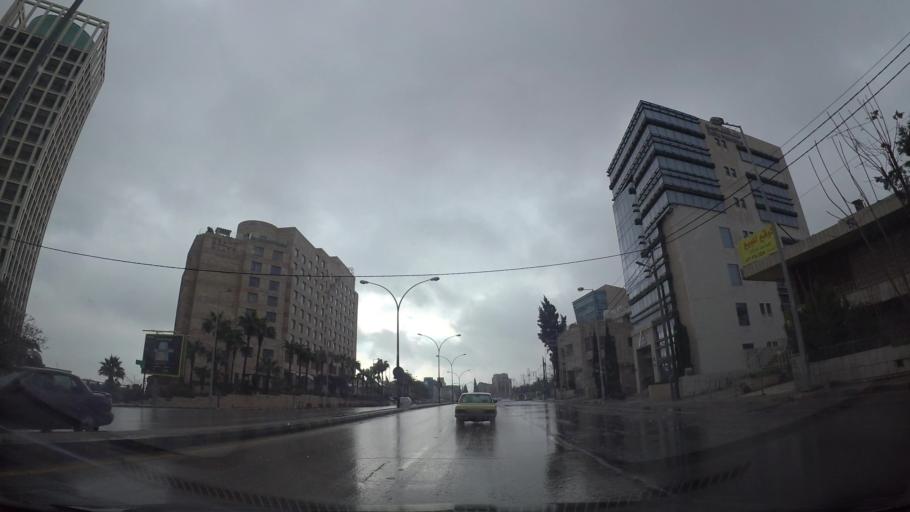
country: JO
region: Amman
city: Amman
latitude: 31.9563
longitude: 35.9084
